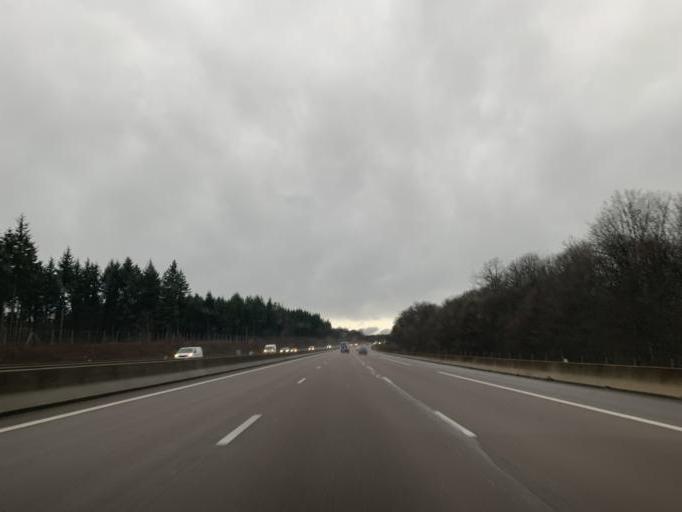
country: FR
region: Bourgogne
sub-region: Departement de la Cote-d'Or
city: Selongey
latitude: 47.6588
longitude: 5.1754
